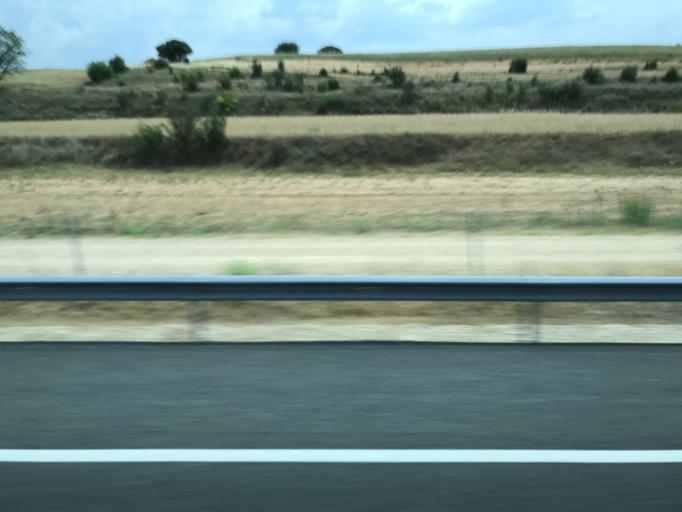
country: ES
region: Castille and Leon
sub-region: Provincia de Burgos
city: Villalba de Duero
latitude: 41.6824
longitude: -3.7243
